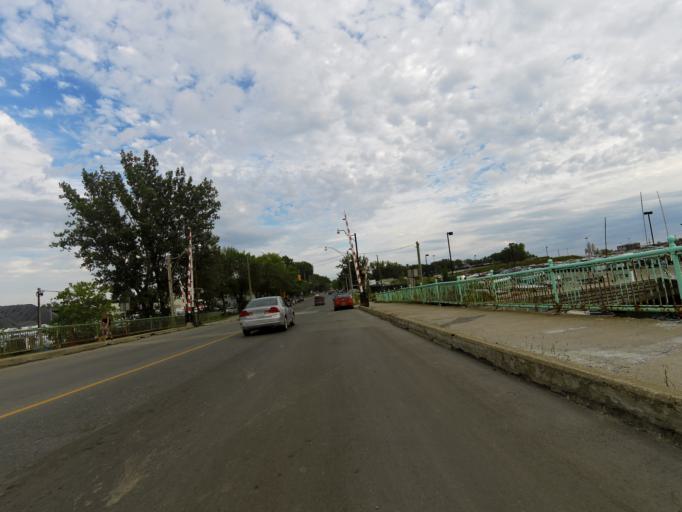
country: CA
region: Ontario
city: Toronto
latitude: 43.6410
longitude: -79.3489
